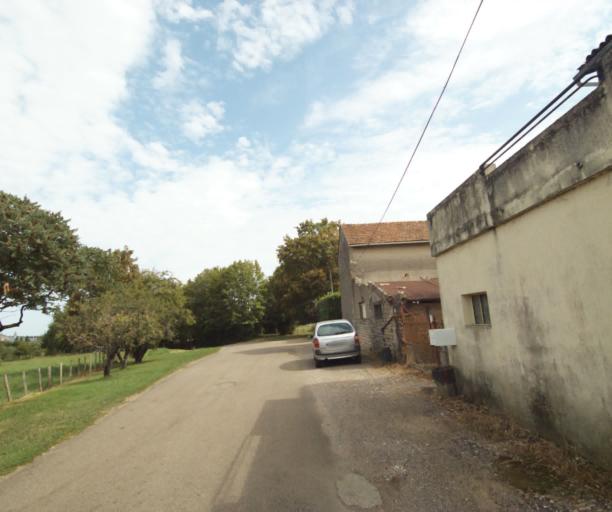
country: FR
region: Bourgogne
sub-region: Departement de Saone-et-Loire
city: Tournus
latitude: 46.5466
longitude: 4.9108
